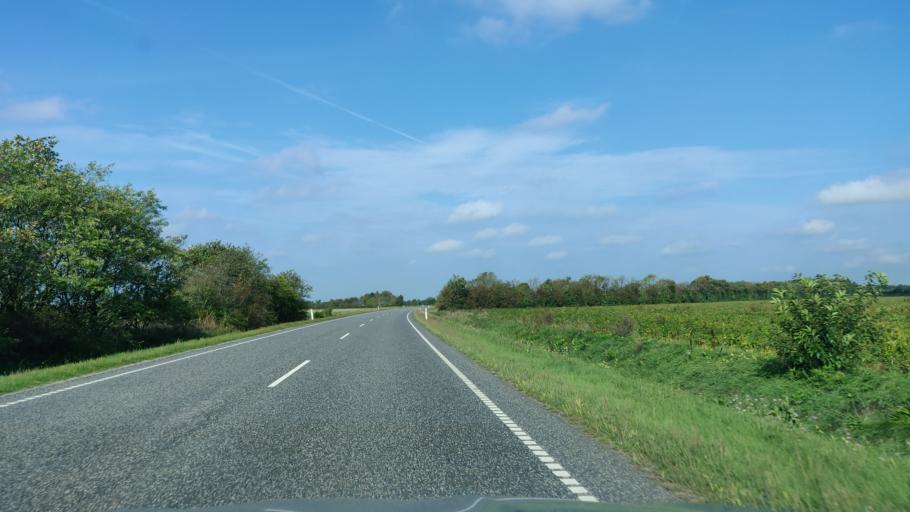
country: DK
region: Central Jutland
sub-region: Herning Kommune
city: Sunds
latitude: 56.2476
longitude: 9.0667
